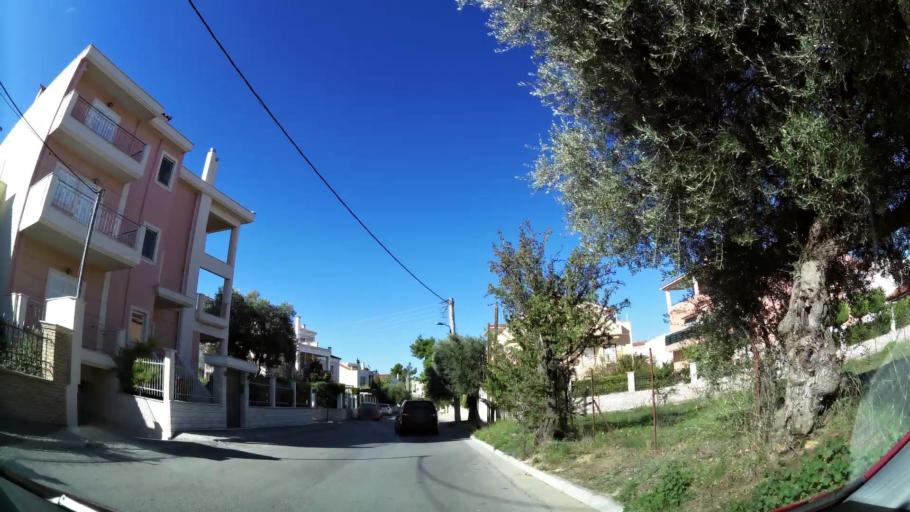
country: GR
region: Attica
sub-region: Nomarchia Athinas
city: Agia Paraskevi
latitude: 38.0196
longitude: 23.8434
